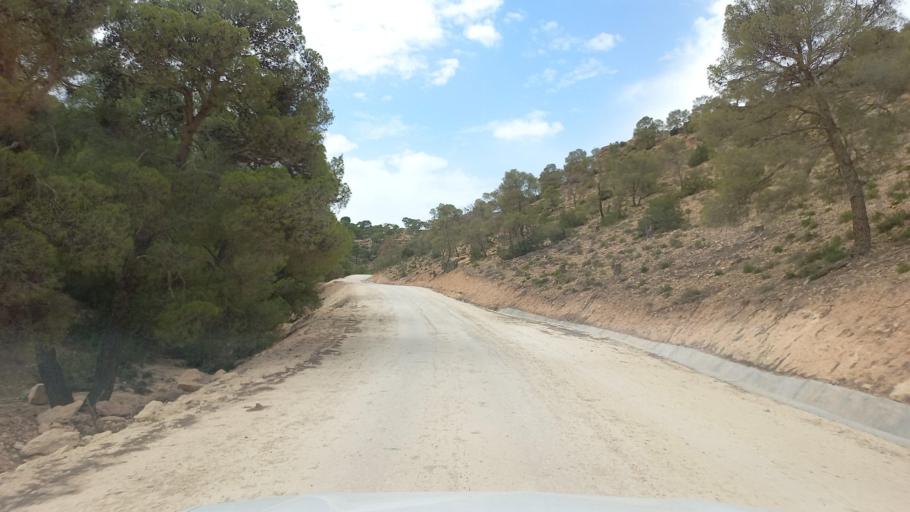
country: TN
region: Al Qasrayn
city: Kasserine
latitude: 35.3774
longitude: 8.8852
